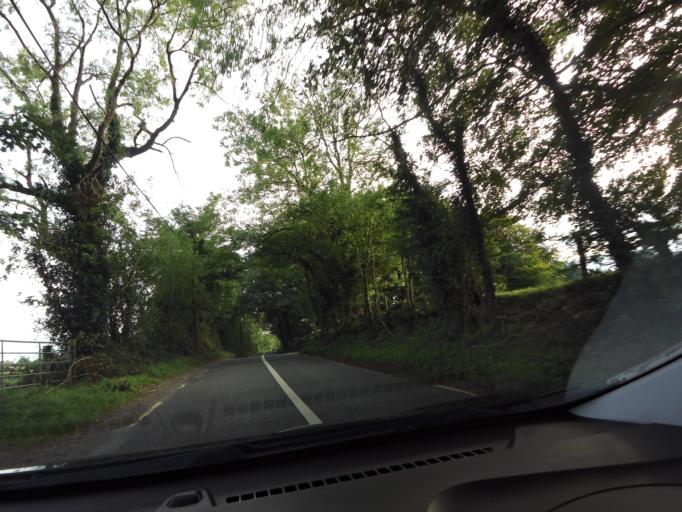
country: IE
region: Connaught
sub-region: County Galway
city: Ballinasloe
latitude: 53.3187
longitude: -8.2791
